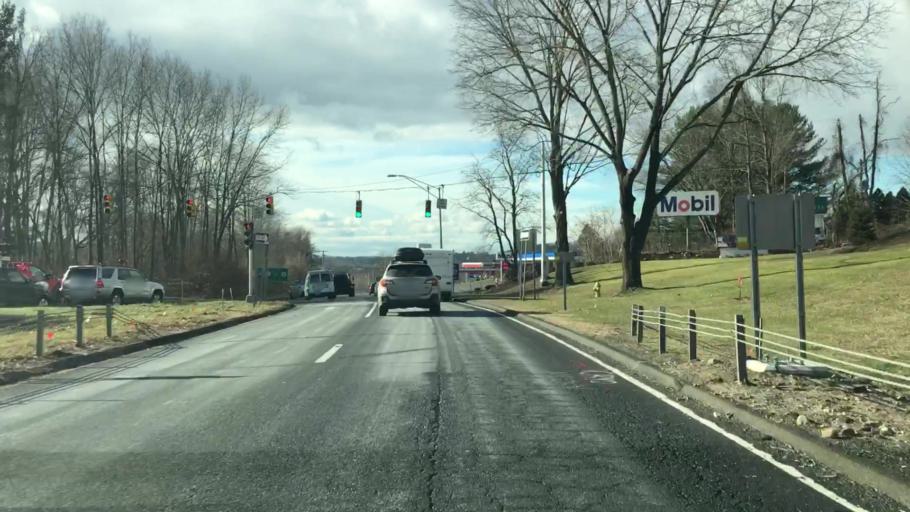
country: US
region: Connecticut
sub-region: Fairfield County
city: Bethel
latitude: 41.4178
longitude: -73.4054
